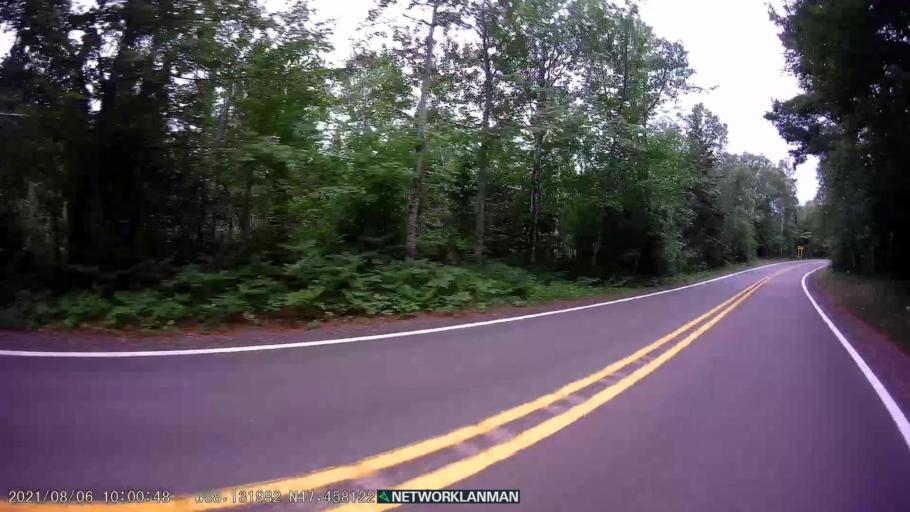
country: US
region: Michigan
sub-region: Keweenaw County
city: Eagle River
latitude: 47.4578
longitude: -88.1326
